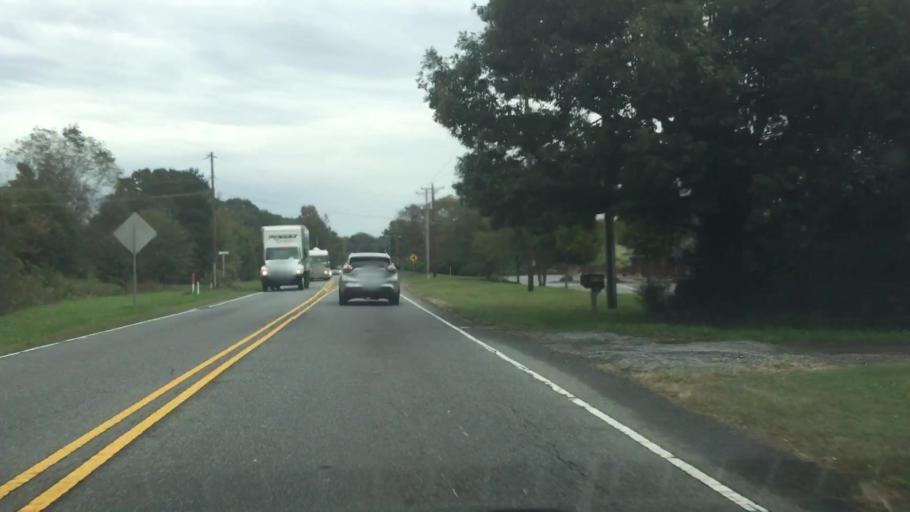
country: US
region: North Carolina
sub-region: Iredell County
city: Mooresville
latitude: 35.6365
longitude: -80.8304
